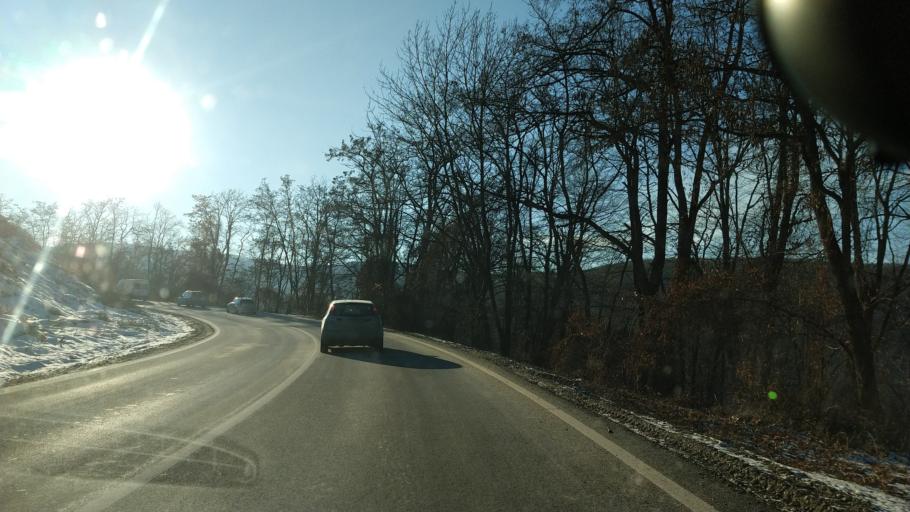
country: RO
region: Bacau
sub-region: Comuna Luizi-Calugara
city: Luizi-Calugara
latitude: 46.5417
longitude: 26.8196
